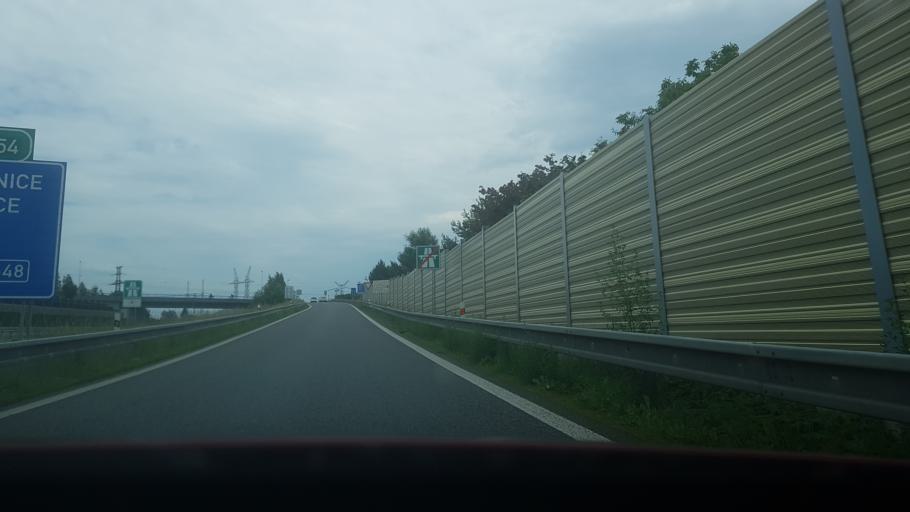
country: CZ
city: Dobra
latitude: 49.6752
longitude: 18.4230
